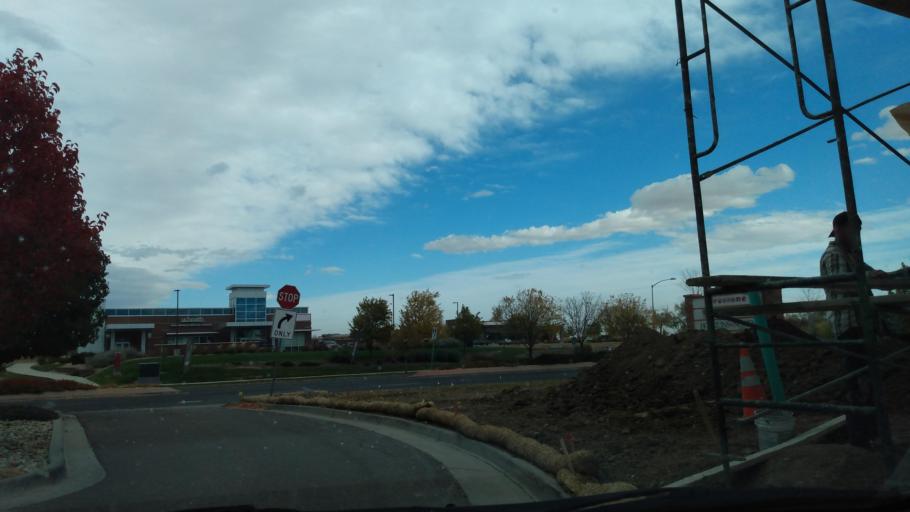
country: US
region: Colorado
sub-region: Adams County
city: Northglenn
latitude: 39.9427
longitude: -104.9987
